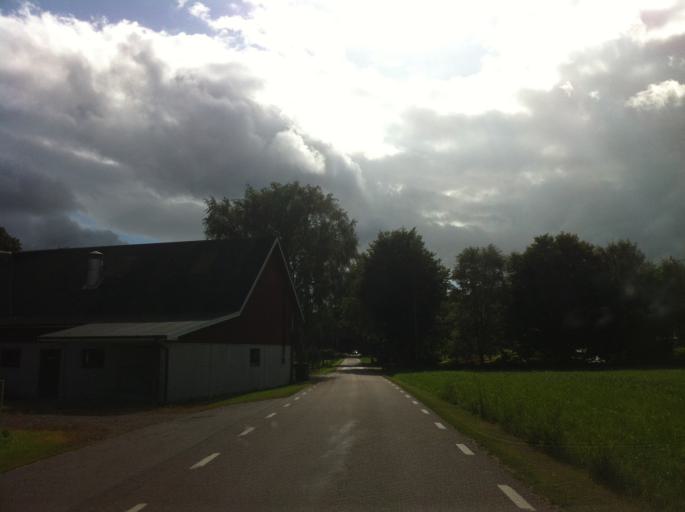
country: SE
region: Skane
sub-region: Bastads Kommun
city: Bastad
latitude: 56.4183
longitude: 12.9154
